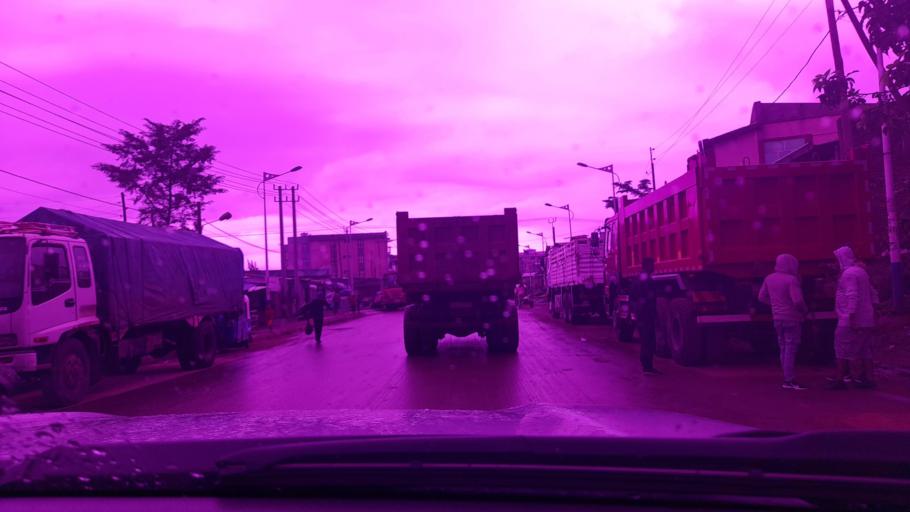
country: ET
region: Oromiya
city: Jima
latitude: 7.6674
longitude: 36.8428
